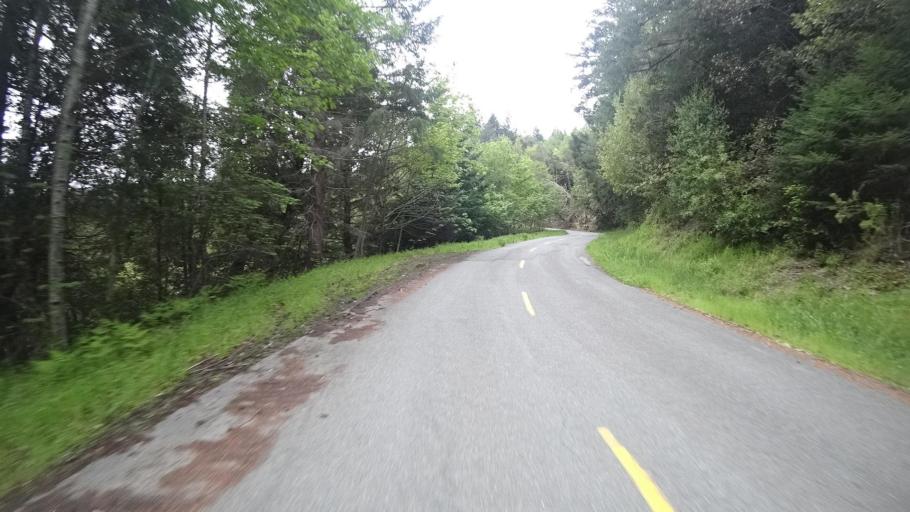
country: US
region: California
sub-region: Humboldt County
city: Blue Lake
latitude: 40.9407
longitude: -123.8417
